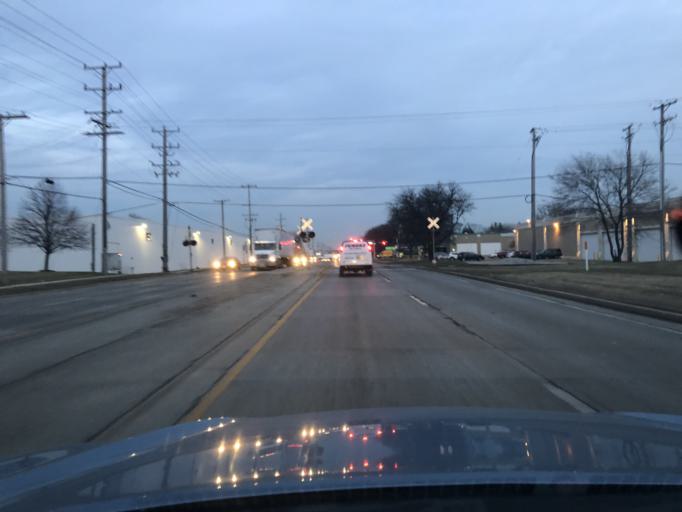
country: US
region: Illinois
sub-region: Cook County
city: Elk Grove Village
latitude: 41.9931
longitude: -87.9726
